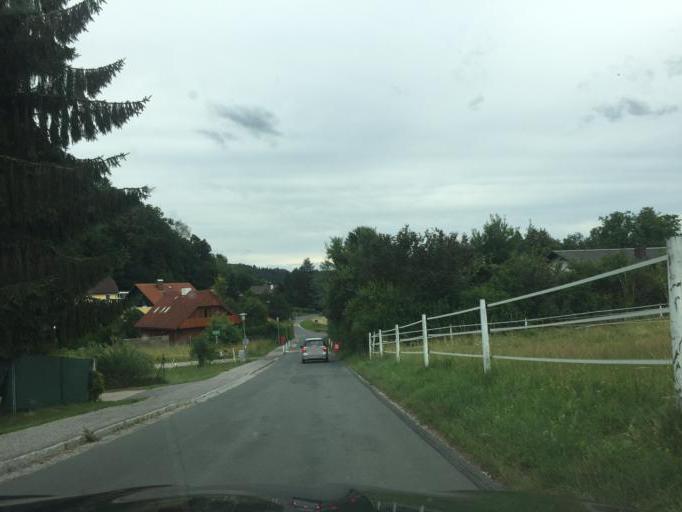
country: AT
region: Styria
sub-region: Politischer Bezirk Graz-Umgebung
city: Hart bei Graz
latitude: 47.0513
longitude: 15.5111
